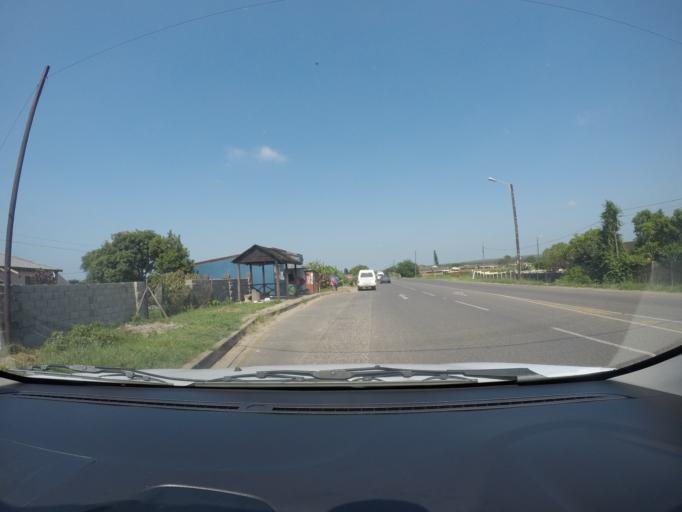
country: ZA
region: KwaZulu-Natal
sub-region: uThungulu District Municipality
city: eSikhawini
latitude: -28.8927
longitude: 31.8859
